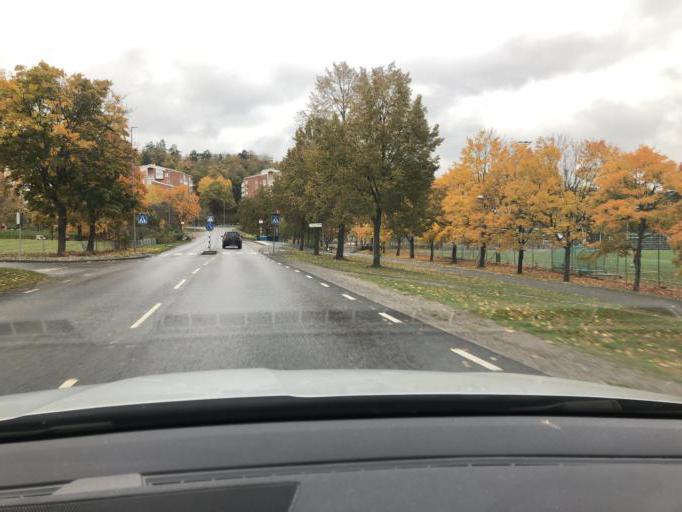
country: SE
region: Stockholm
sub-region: Botkyrka Kommun
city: Alby
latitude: 59.2366
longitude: 17.8519
